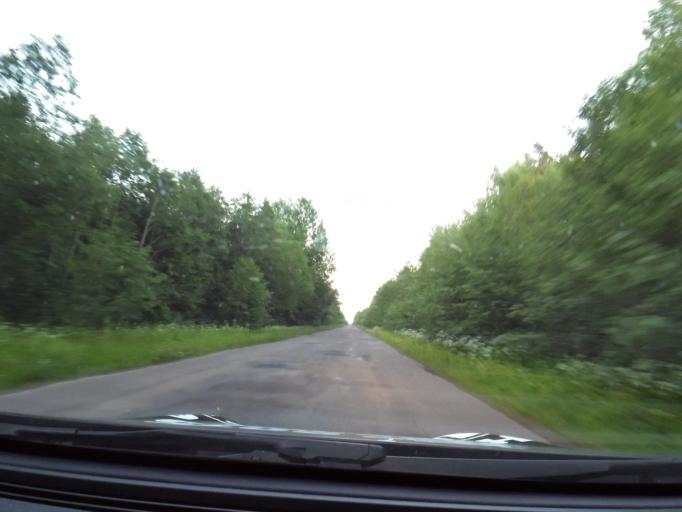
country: RU
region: Leningrad
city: Voznesen'ye
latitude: 60.8322
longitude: 35.6833
